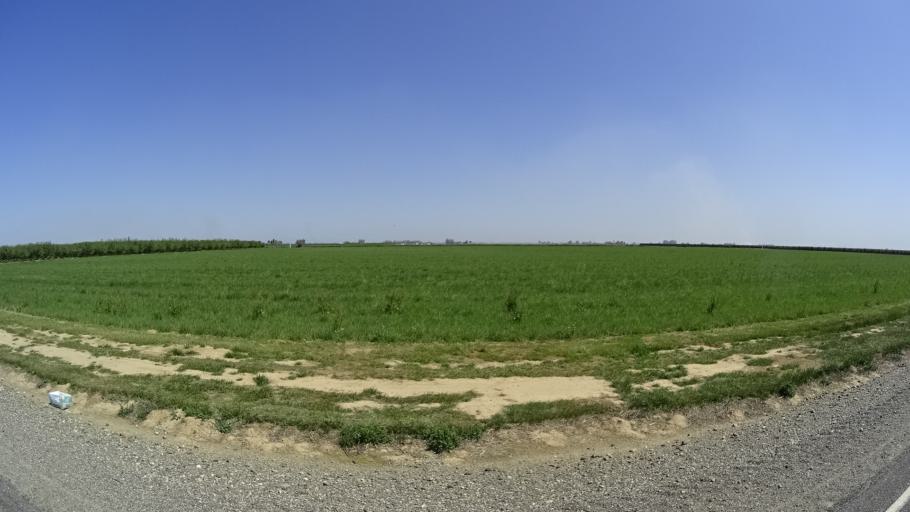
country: US
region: California
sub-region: Glenn County
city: Willows
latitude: 39.5702
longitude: -122.1373
